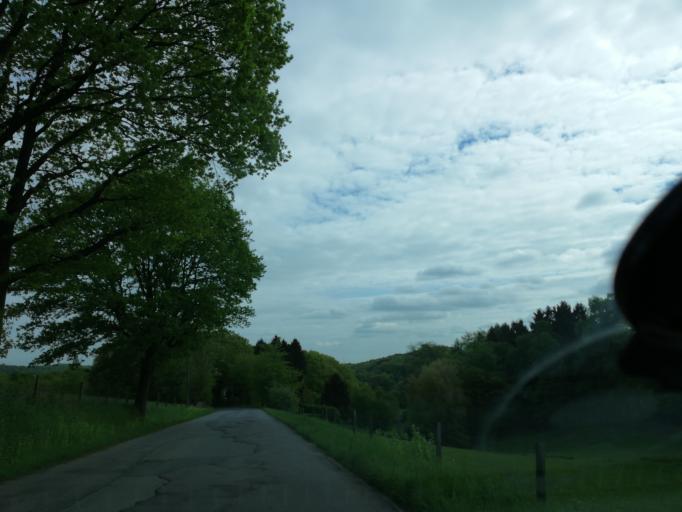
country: DE
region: North Rhine-Westphalia
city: Gevelsberg
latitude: 51.3588
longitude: 7.3055
